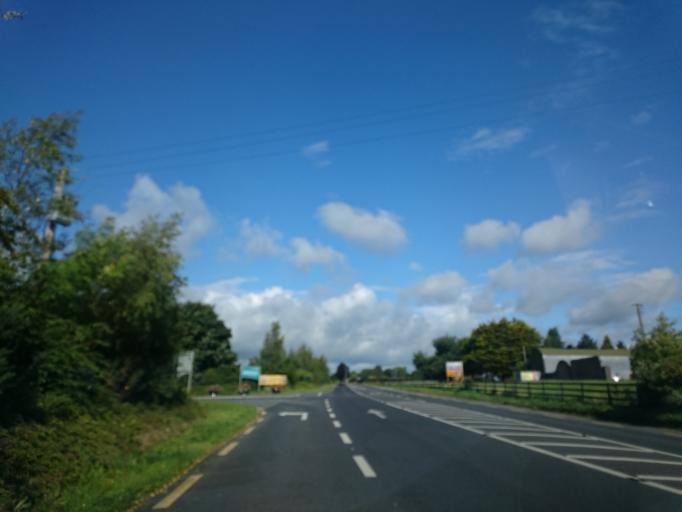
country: IE
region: Leinster
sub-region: Kilkenny
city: Kilkenny
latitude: 52.6956
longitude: -7.2627
